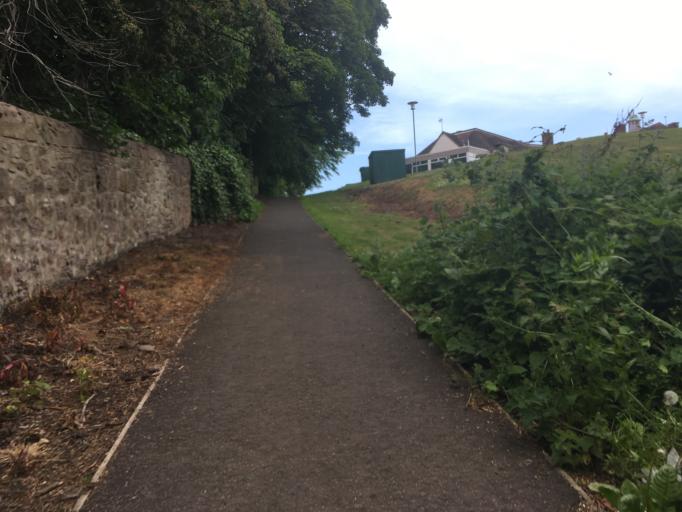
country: GB
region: Scotland
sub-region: Edinburgh
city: Edinburgh
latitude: 55.9269
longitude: -3.2001
